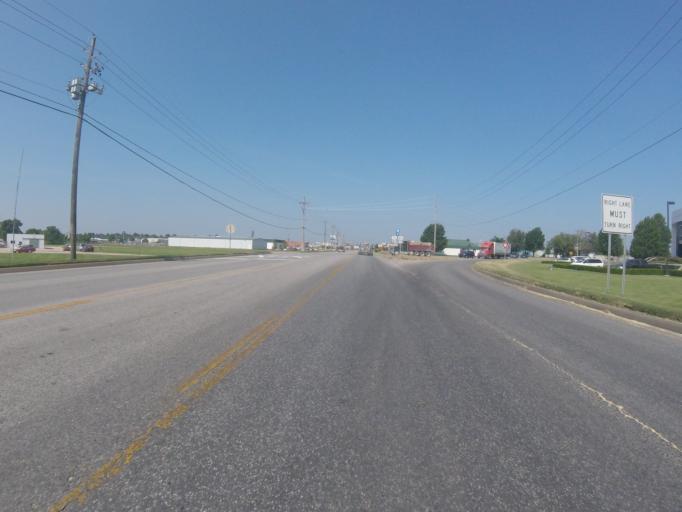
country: US
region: Arkansas
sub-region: Washington County
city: Springdale
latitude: 36.1673
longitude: -94.1373
